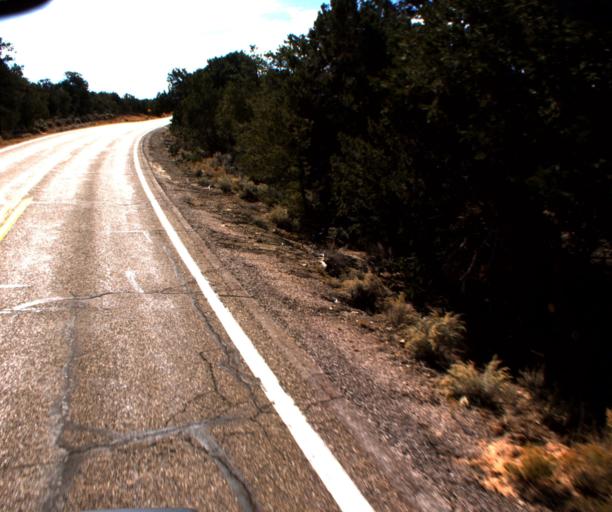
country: US
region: Arizona
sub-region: Navajo County
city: Kayenta
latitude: 36.6533
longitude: -110.5189
